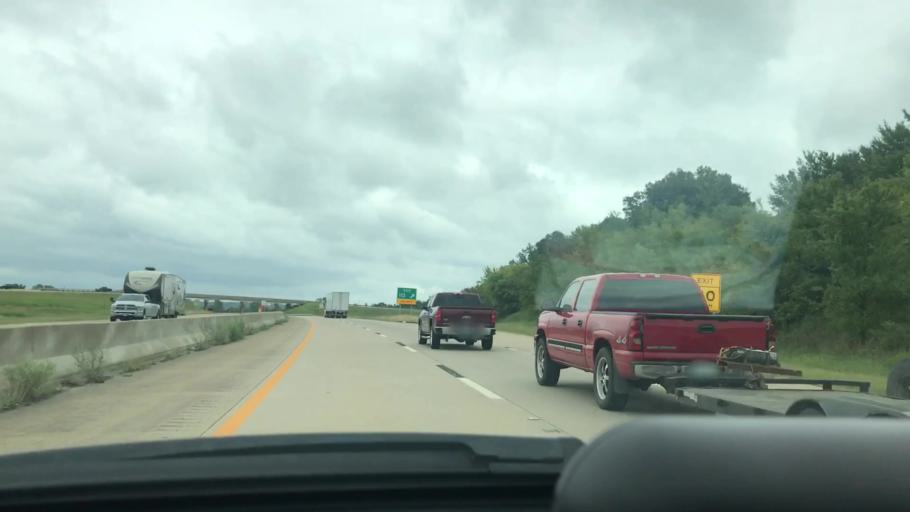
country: US
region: Oklahoma
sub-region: McIntosh County
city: Eufaula
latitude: 35.2140
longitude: -95.6134
